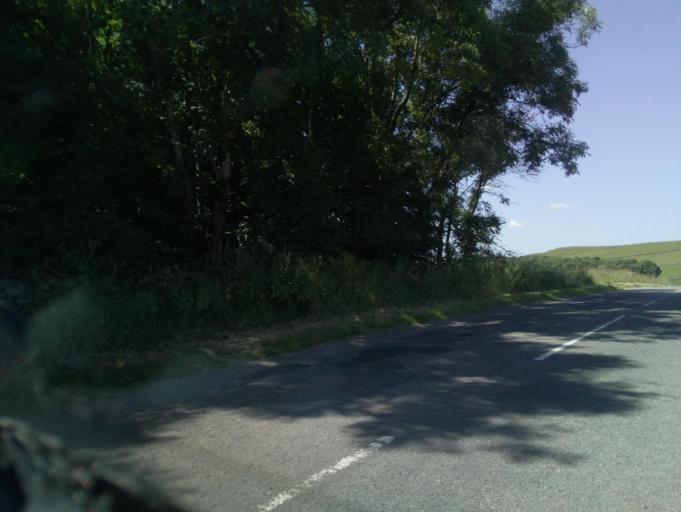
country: GB
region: England
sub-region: Derbyshire
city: Tideswell
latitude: 53.2747
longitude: -1.8312
